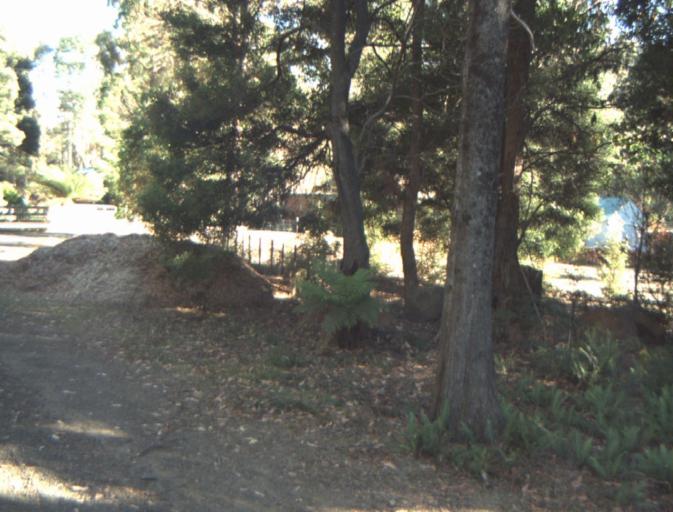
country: AU
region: Tasmania
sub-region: Launceston
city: Mayfield
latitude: -41.3008
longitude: 147.1896
